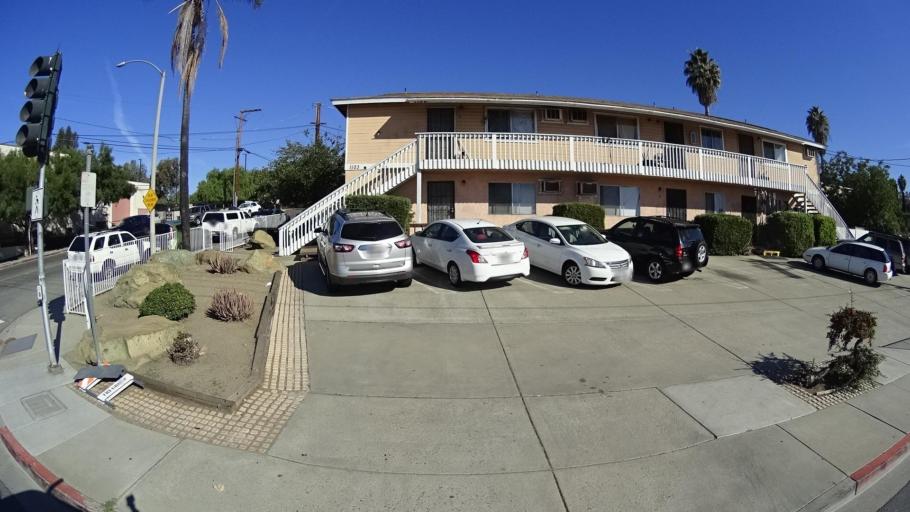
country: US
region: California
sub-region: San Diego County
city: La Presa
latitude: 32.7149
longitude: -117.0094
